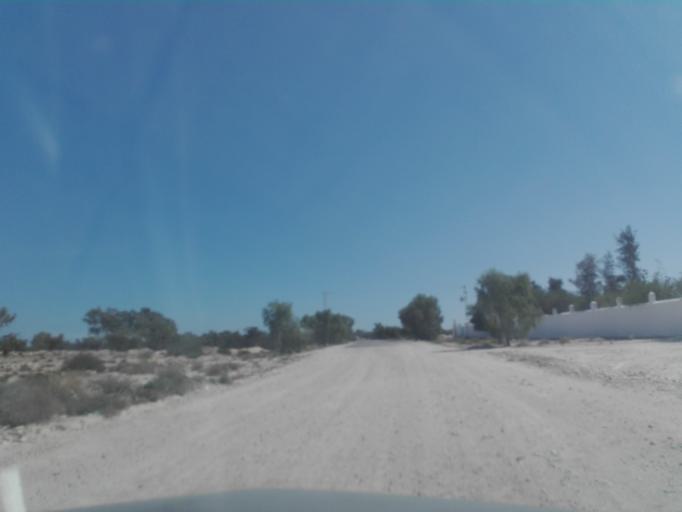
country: TN
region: Qabis
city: Gabes
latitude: 33.8727
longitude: 10.0326
